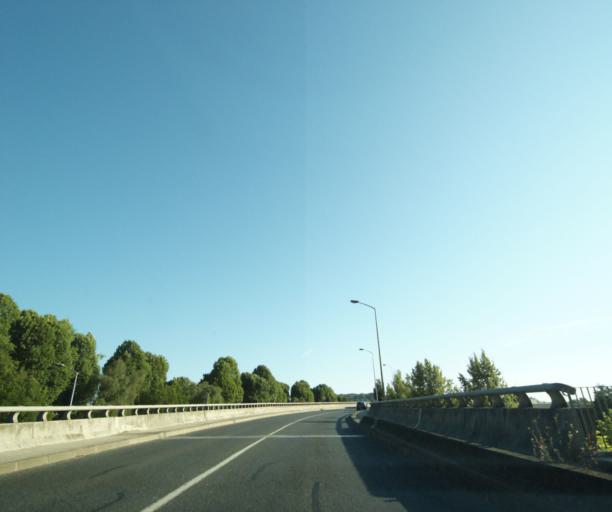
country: FR
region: Ile-de-France
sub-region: Departement de Seine-et-Marne
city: Montereau-Fault-Yonne
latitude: 48.3793
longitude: 2.9571
